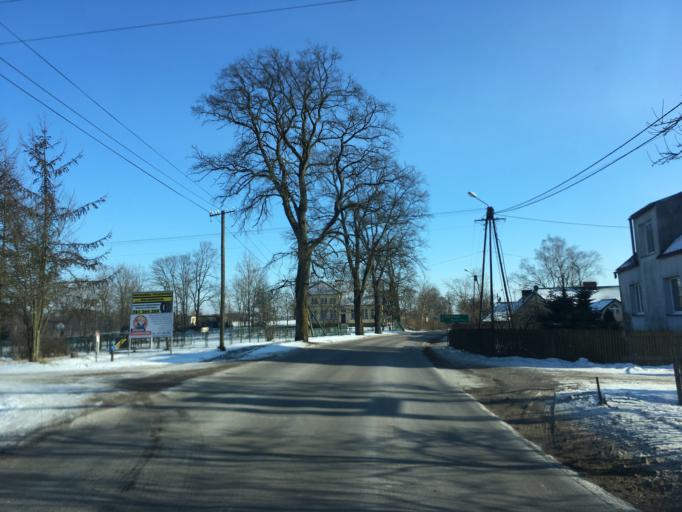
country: PL
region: Pomeranian Voivodeship
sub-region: Powiat koscierski
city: Koscierzyna
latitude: 54.0715
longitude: 18.0090
